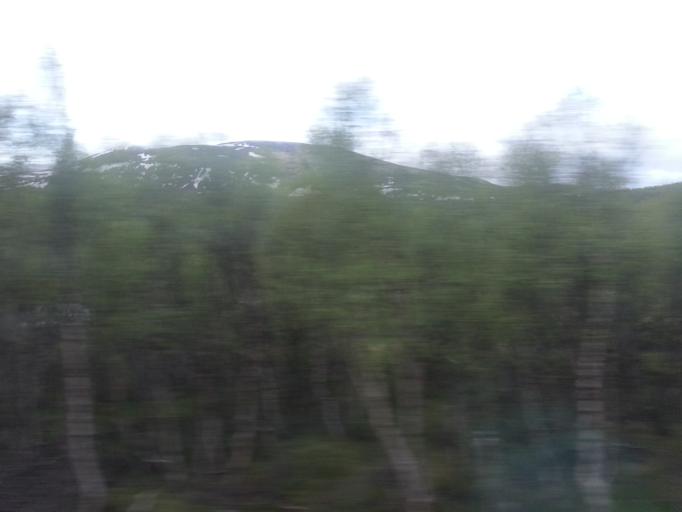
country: NO
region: Oppland
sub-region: Dovre
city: Dovre
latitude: 62.1762
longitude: 9.4249
